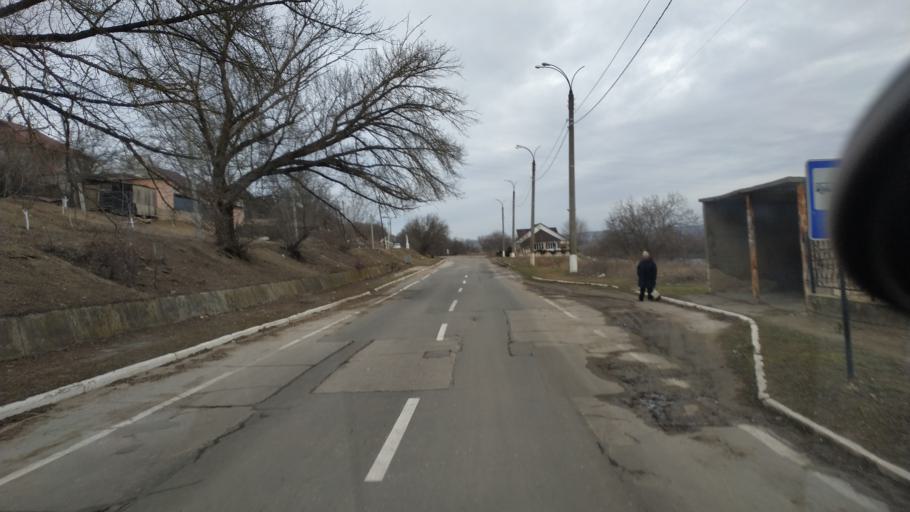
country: MD
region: Criuleni
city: Criuleni
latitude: 47.2229
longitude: 29.1631
